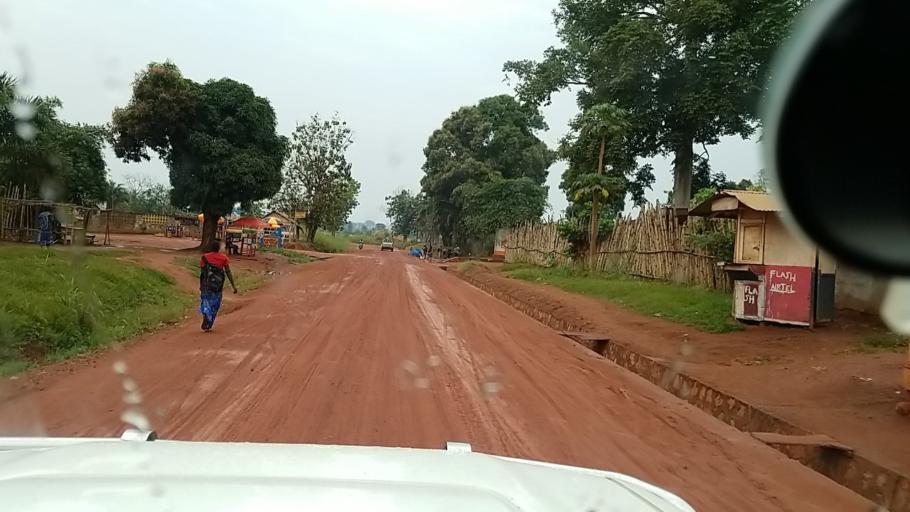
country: CD
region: Equateur
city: Gemena
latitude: 3.2371
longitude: 19.7799
